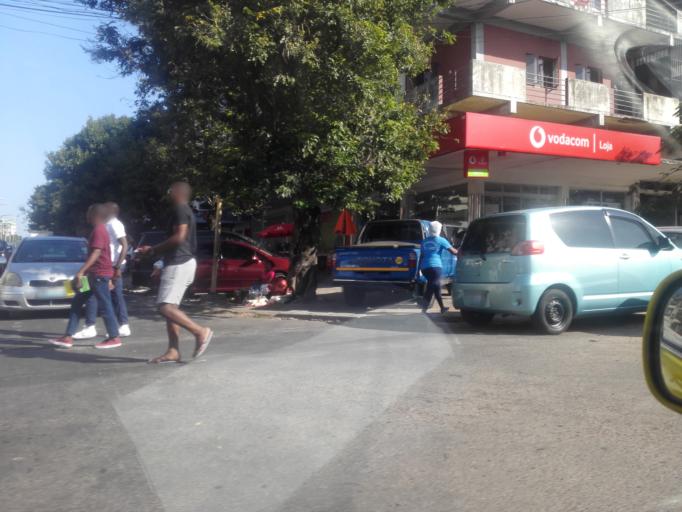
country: MZ
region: Maputo City
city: Maputo
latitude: -25.9615
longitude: 32.5826
